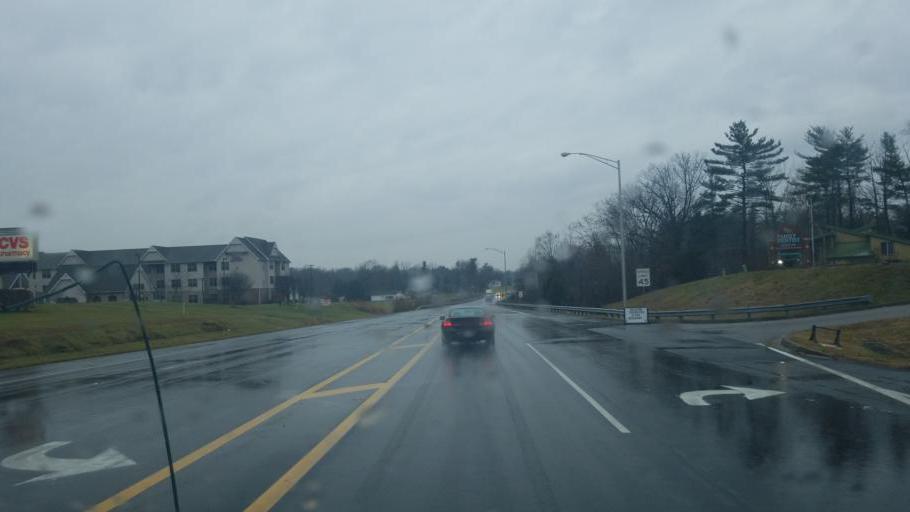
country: US
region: Indiana
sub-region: Bartholomew County
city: Columbus
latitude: 39.1996
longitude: -85.9738
